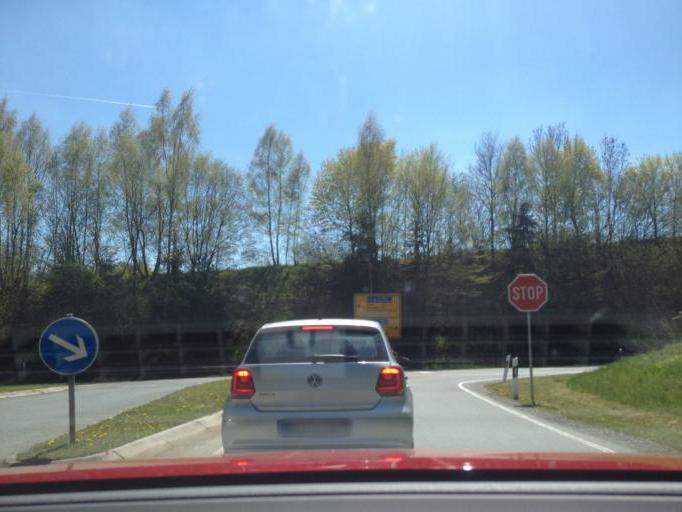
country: DE
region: Bavaria
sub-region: Upper Franconia
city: Schwarzenbach an der Saale
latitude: 50.2293
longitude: 11.9311
